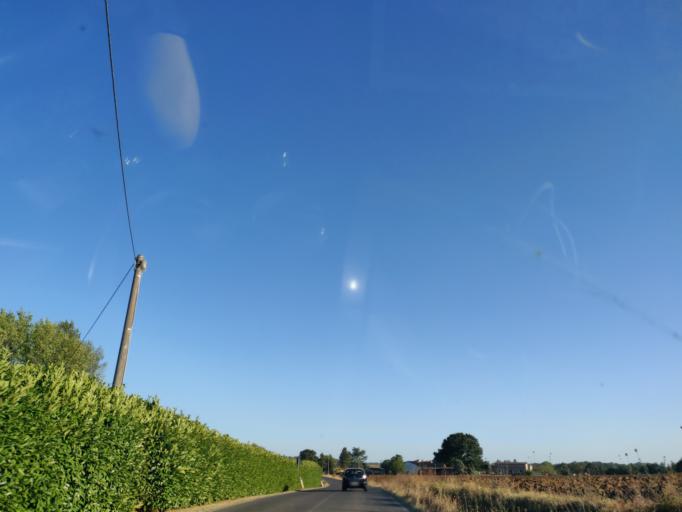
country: IT
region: Latium
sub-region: Provincia di Viterbo
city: Acquapendente
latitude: 42.7216
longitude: 11.8743
